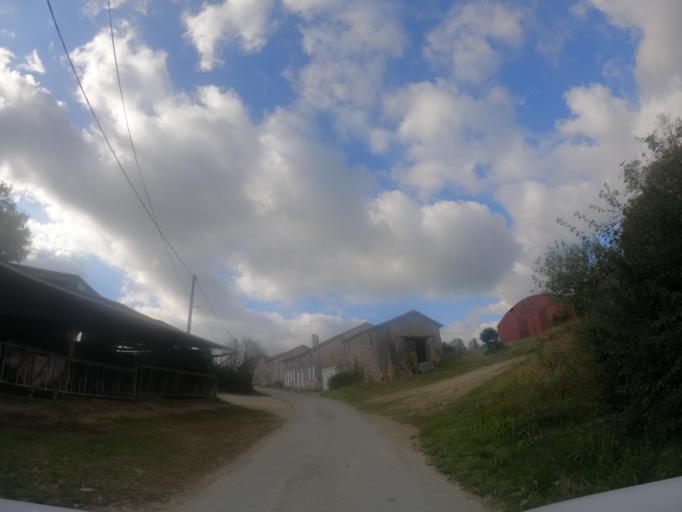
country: FR
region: Poitou-Charentes
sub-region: Departement des Deux-Sevres
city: Courlay
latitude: 46.7969
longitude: -0.5948
